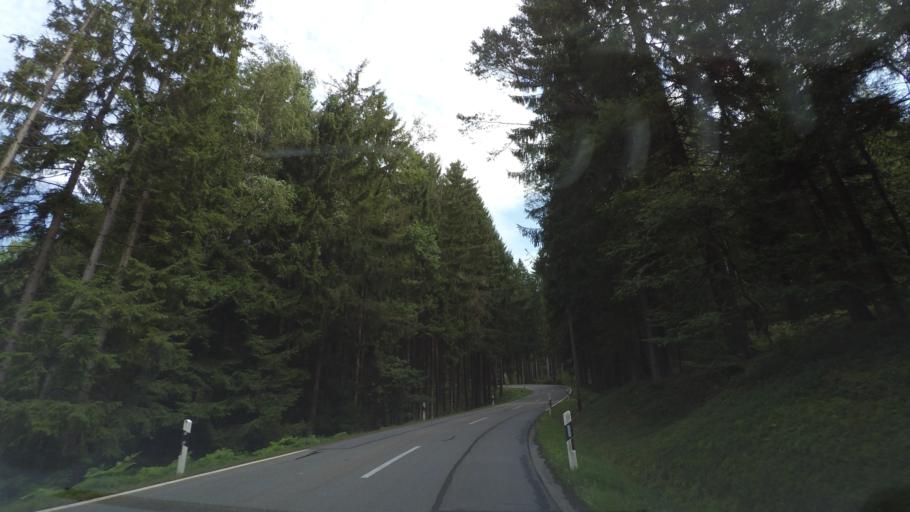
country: DE
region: Bavaria
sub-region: Lower Bavaria
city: Arnbruck
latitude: 49.1381
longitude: 13.0032
